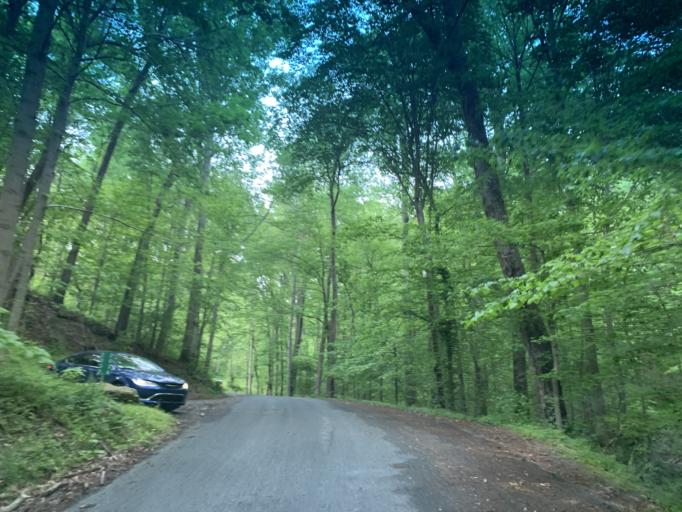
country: US
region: Pennsylvania
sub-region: York County
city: Susquehanna Trails
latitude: 39.7036
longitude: -76.2614
